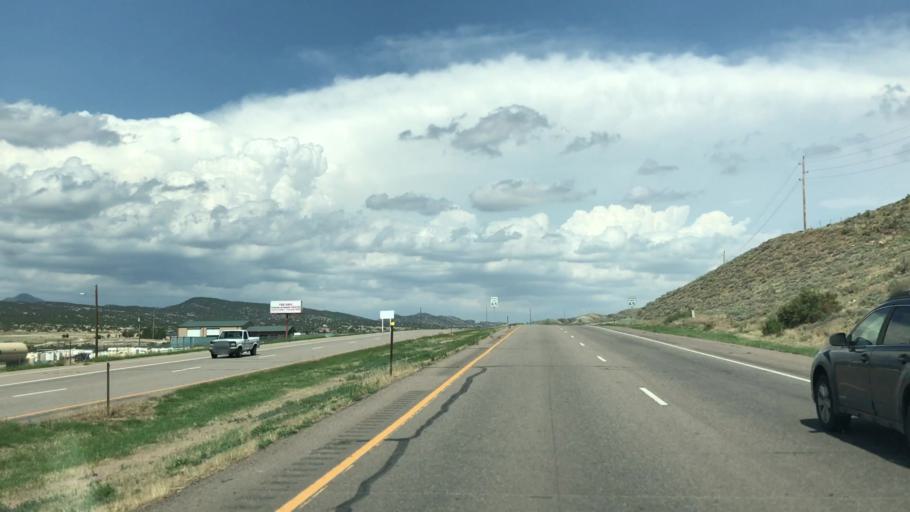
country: US
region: Colorado
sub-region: Fremont County
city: Lincoln Park
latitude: 38.4489
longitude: -105.1719
